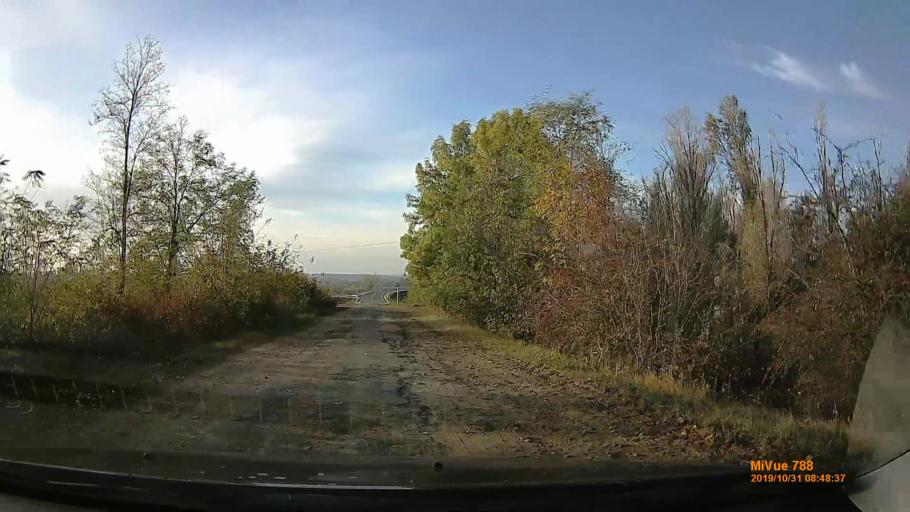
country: HU
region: Pest
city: Albertirsa
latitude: 47.2742
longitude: 19.6065
